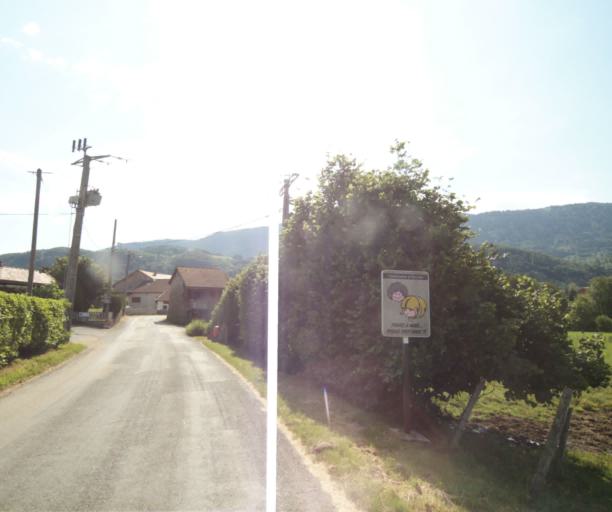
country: FR
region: Rhone-Alpes
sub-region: Departement de la Haute-Savoie
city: Armoy
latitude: 46.3269
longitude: 6.4957
